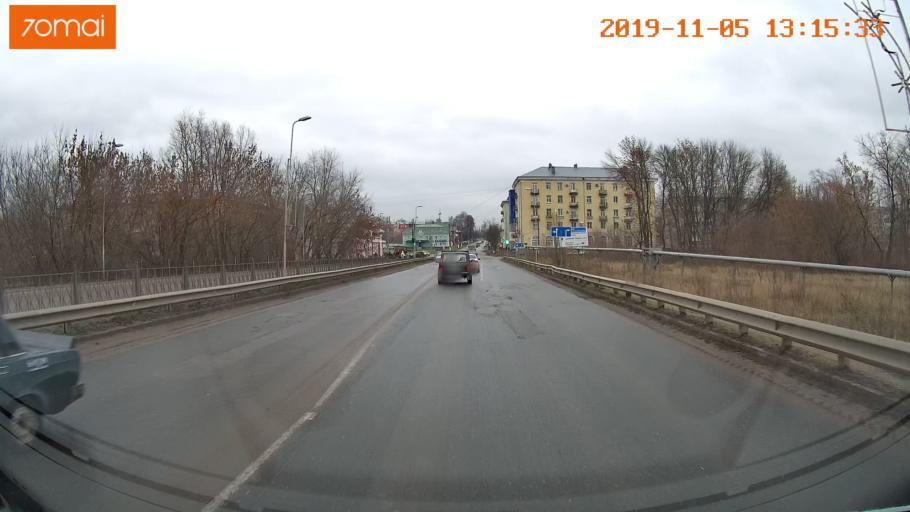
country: RU
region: Ivanovo
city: Shuya
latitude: 56.8508
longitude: 41.3661
